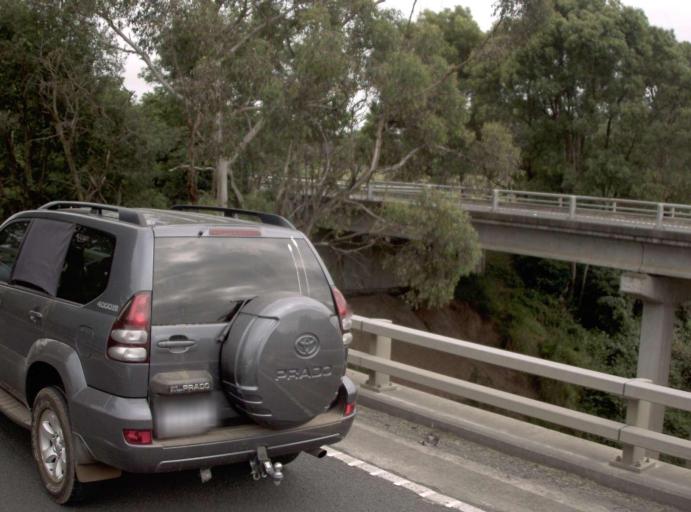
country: AU
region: Victoria
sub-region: Cardinia
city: Bunyip
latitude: -38.0826
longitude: 145.7521
